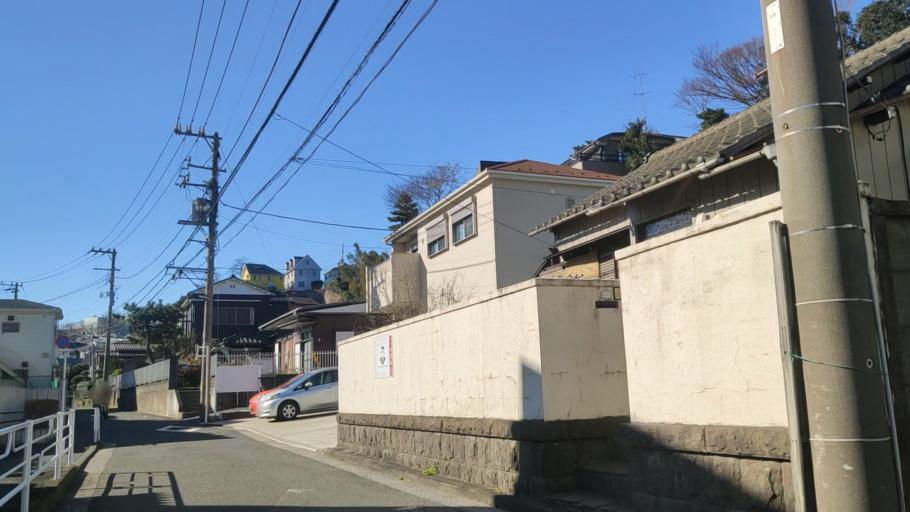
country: JP
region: Kanagawa
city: Yokohama
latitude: 35.4278
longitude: 139.6565
